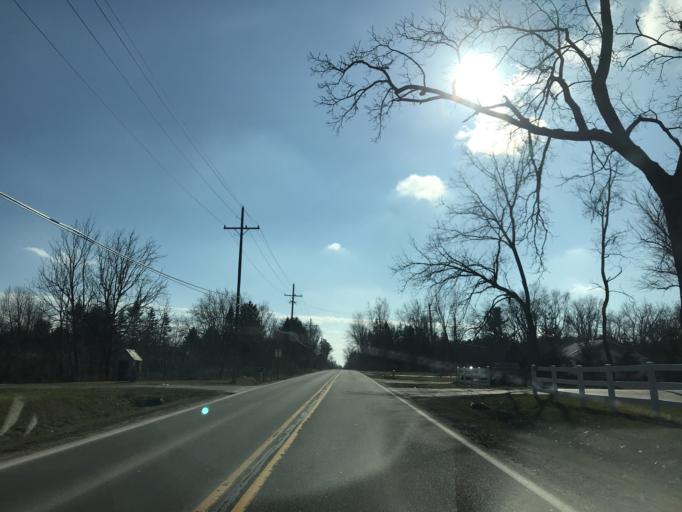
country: US
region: Michigan
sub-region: Oakland County
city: South Lyon
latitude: 42.4502
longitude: -83.6959
